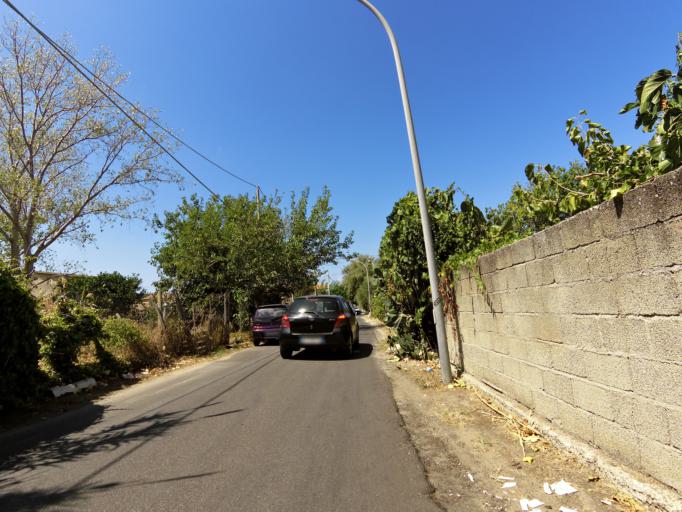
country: IT
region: Calabria
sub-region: Provincia di Vibo-Valentia
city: Santa Domenica
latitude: 38.6680
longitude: 15.8727
